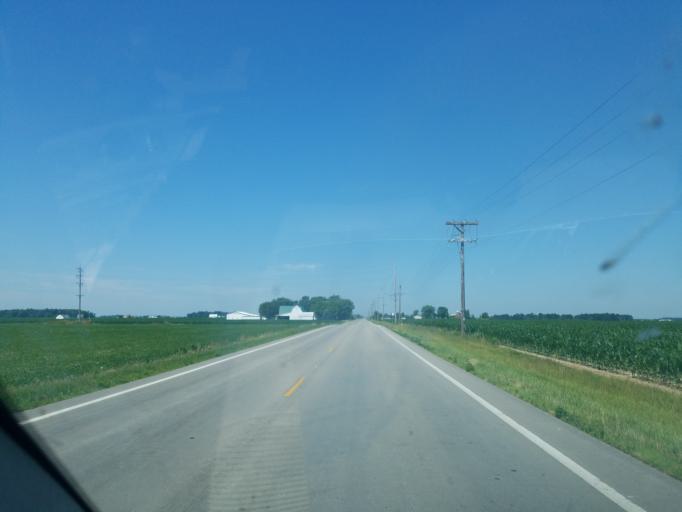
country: US
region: Ohio
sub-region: Auglaize County
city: New Bremen
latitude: 40.4368
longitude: -84.4034
